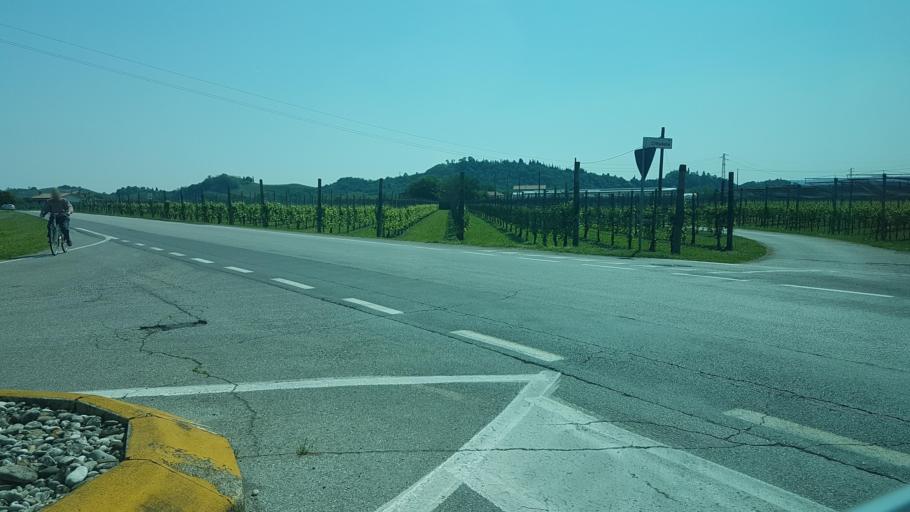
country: IT
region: Veneto
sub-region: Provincia di Treviso
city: Bigolino
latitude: 45.8698
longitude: 12.0187
